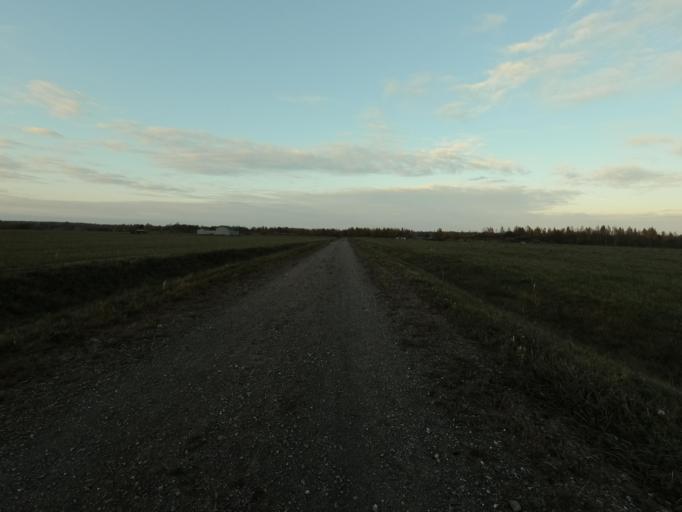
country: RU
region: Leningrad
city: Mga
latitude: 59.7874
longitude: 31.1992
